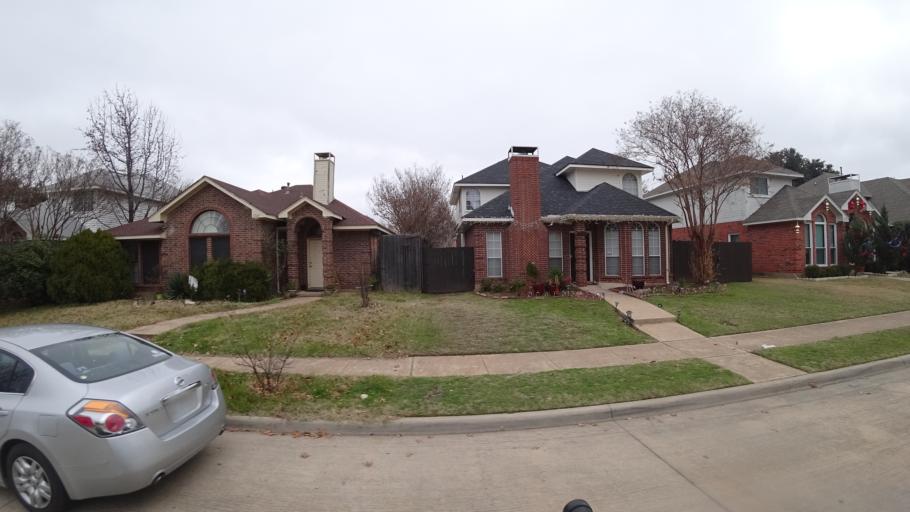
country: US
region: Texas
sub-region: Denton County
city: Lewisville
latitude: 33.0250
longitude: -97.0323
